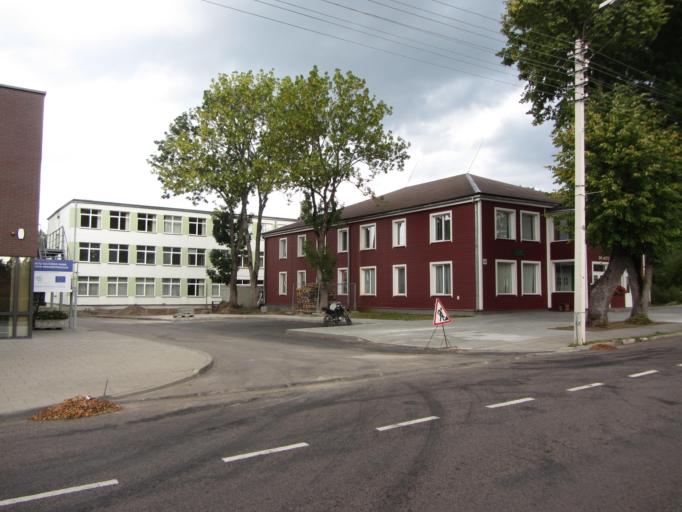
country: LT
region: Panevezys
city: Rokiskis
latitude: 55.7502
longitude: 25.8440
